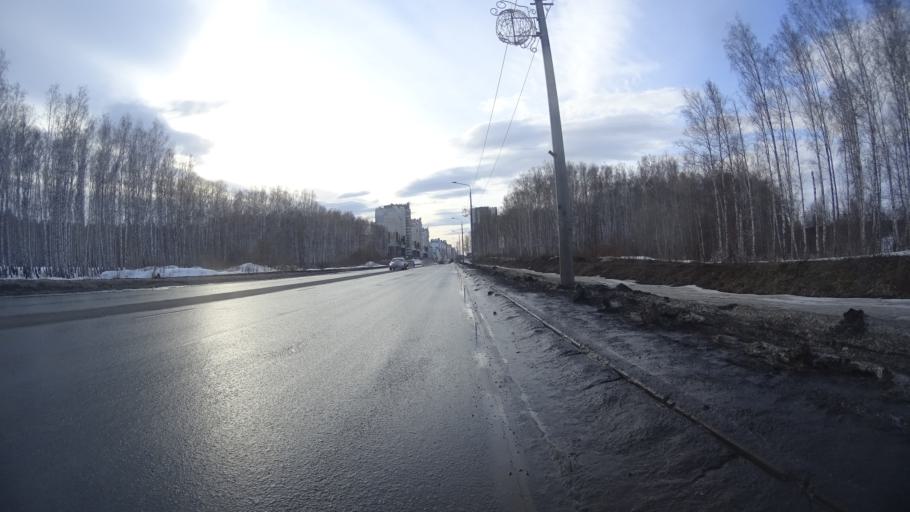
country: RU
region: Chelyabinsk
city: Roshchino
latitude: 55.2086
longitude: 61.3123
